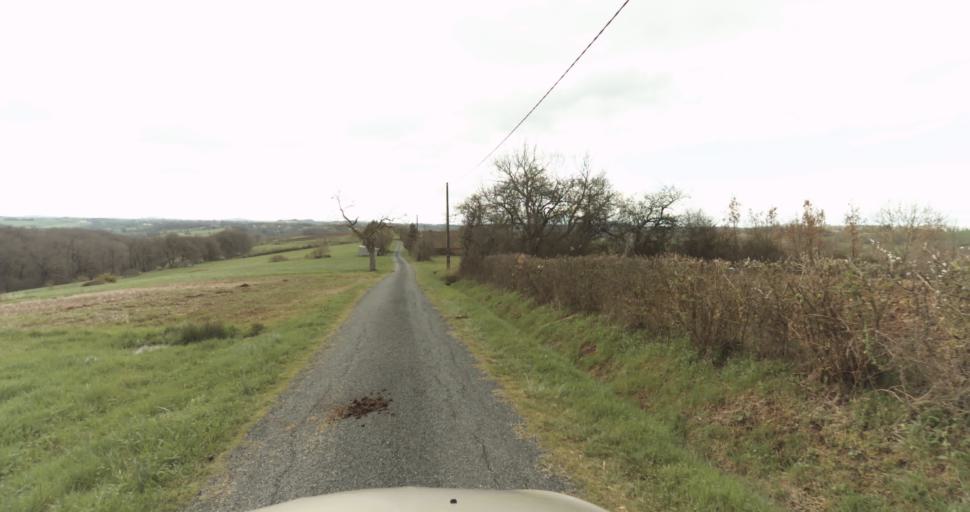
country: FR
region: Midi-Pyrenees
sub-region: Departement du Tarn
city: Frejairolles
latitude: 43.8564
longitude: 2.2195
